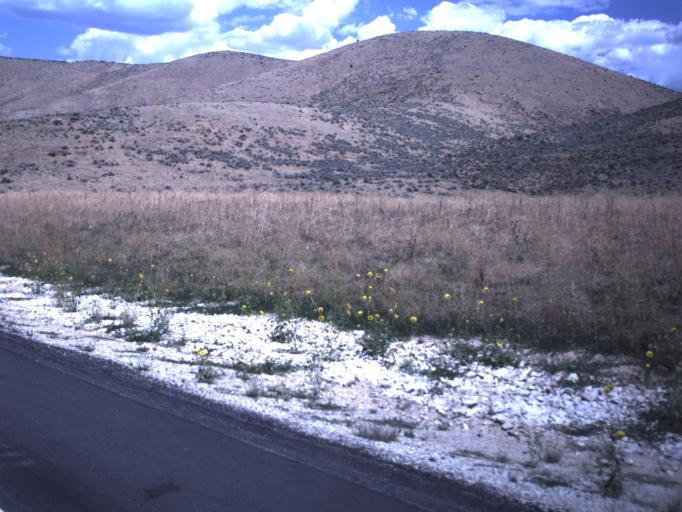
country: US
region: Utah
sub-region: Wasatch County
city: Midway
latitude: 40.4212
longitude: -111.4894
